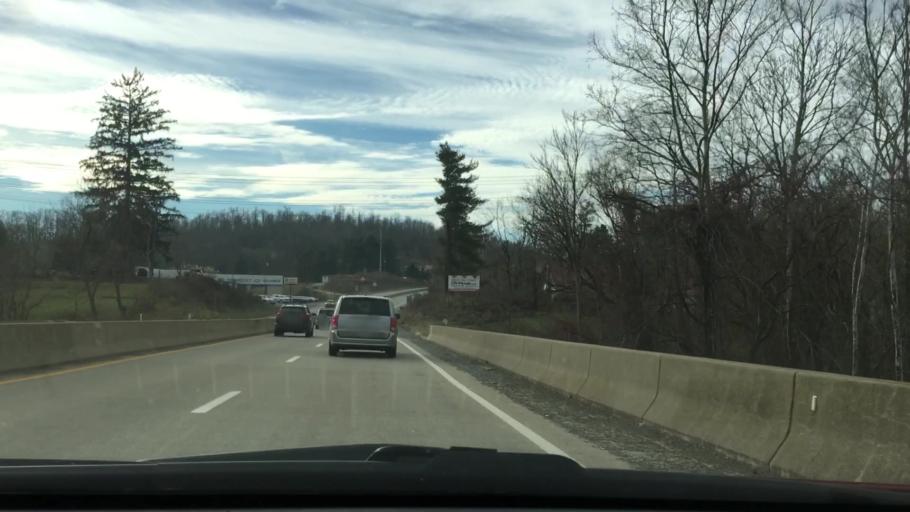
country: US
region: Pennsylvania
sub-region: Fayette County
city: Masontown
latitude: 39.8649
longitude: -79.8942
